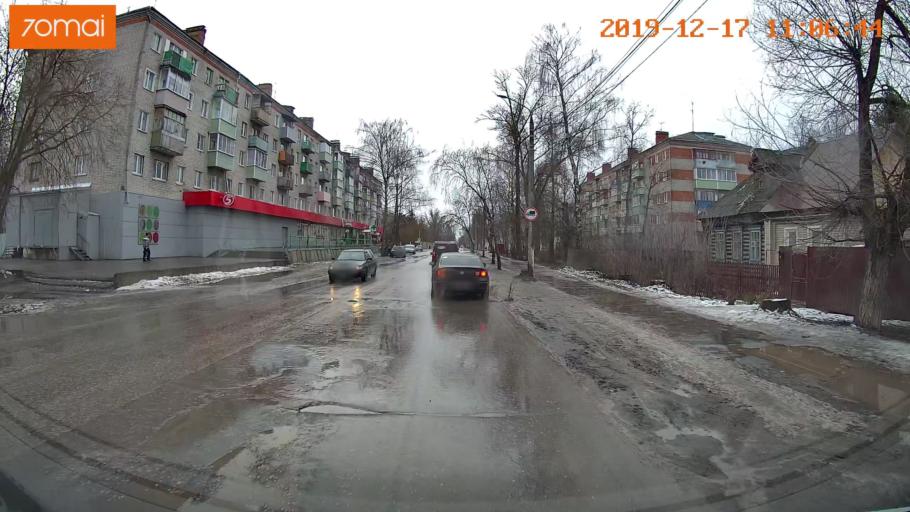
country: RU
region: Vladimir
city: Gus'-Khrustal'nyy
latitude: 55.6144
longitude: 40.6446
